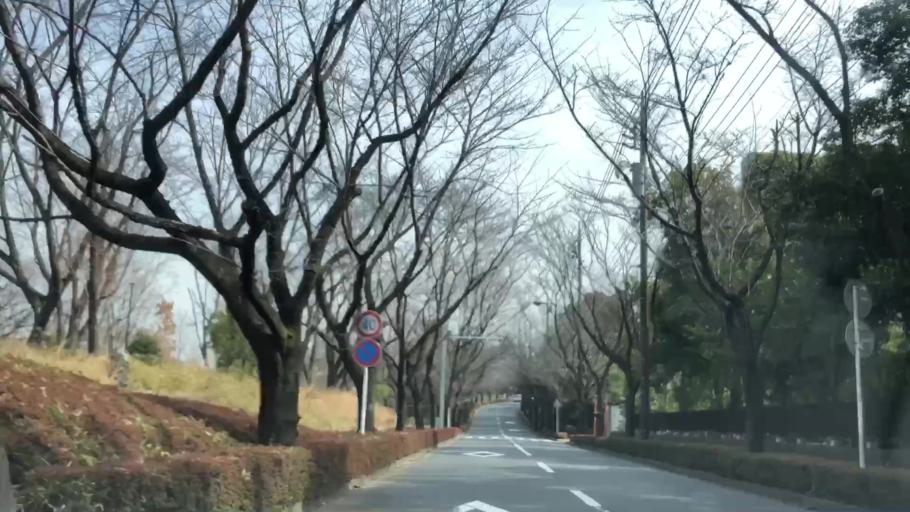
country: JP
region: Saitama
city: Wako
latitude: 35.7756
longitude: 139.6030
